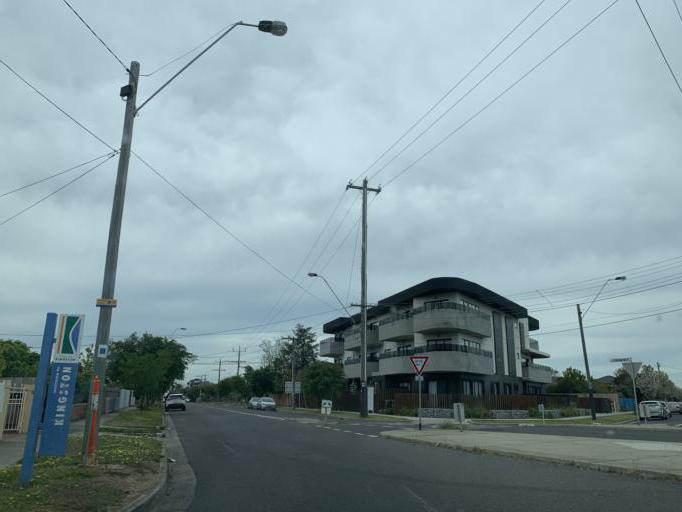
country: AU
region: Victoria
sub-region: Bayside
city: Highett
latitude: -37.9447
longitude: 145.0395
